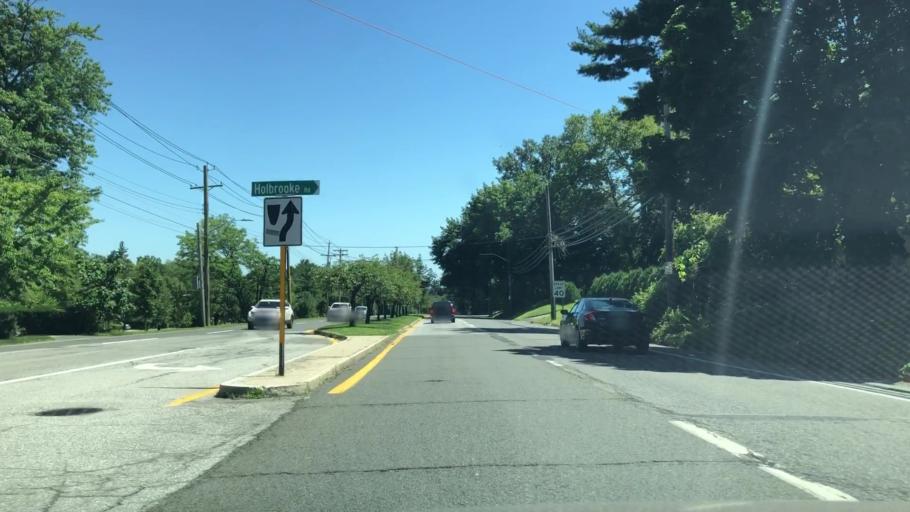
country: US
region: New York
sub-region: Westchester County
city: White Plains
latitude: 41.0023
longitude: -73.7494
